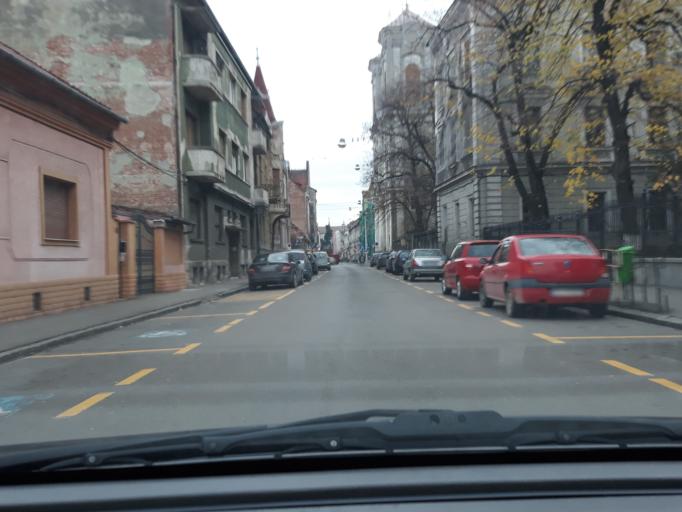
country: RO
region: Bihor
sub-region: Comuna Biharea
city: Oradea
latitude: 47.0609
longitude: 21.9309
